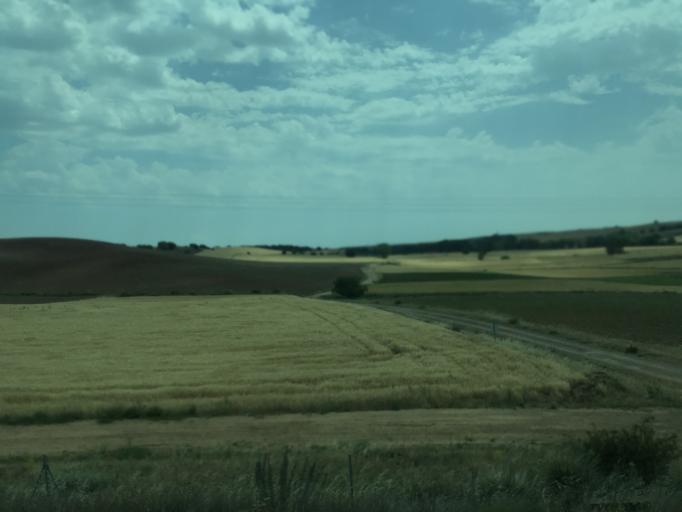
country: ES
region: Castille and Leon
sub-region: Provincia de Burgos
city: Madrigalejo del Monte
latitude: 42.1091
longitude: -3.7188
